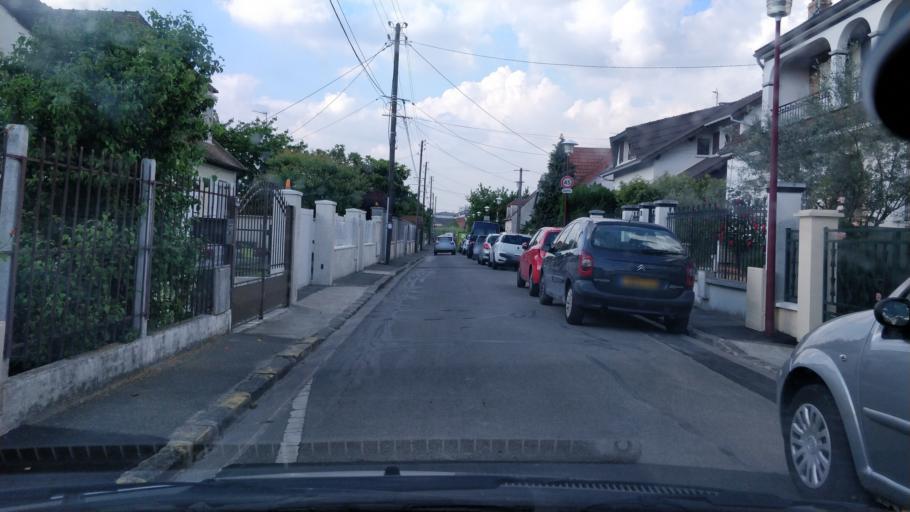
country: FR
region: Ile-de-France
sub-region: Departement de Seine-Saint-Denis
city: Bondy
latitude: 48.8913
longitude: 2.4855
